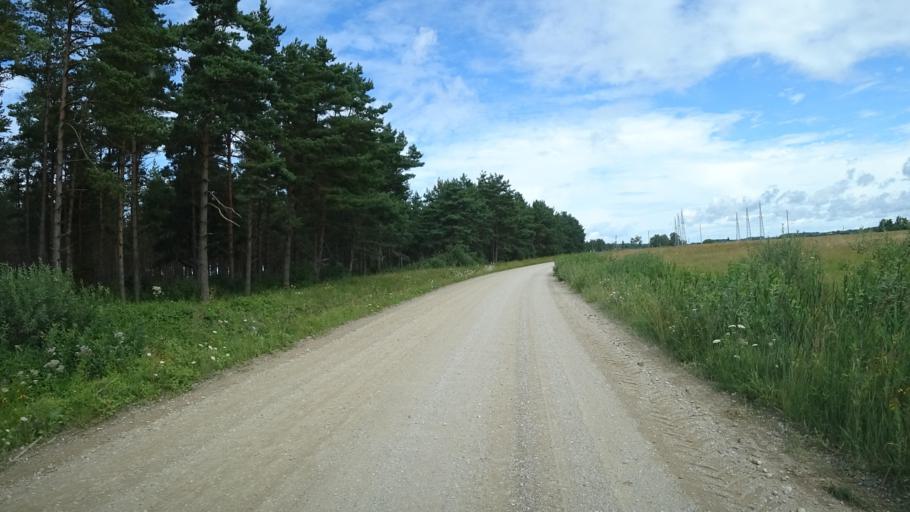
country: LV
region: Liepaja
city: Vec-Liepaja
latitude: 56.6365
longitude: 21.0456
